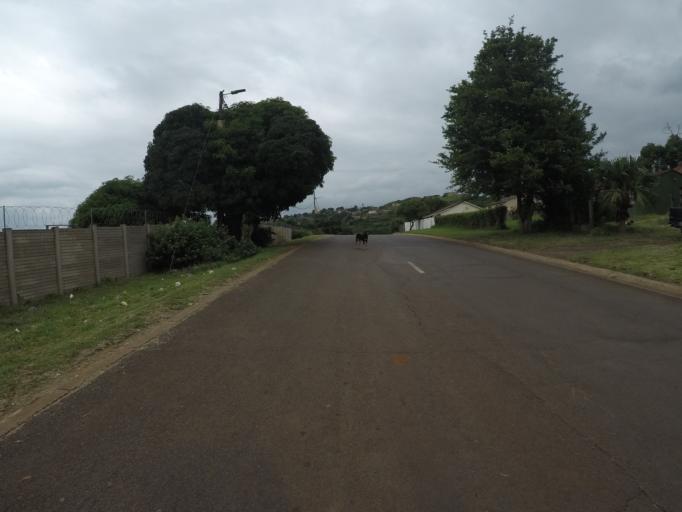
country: ZA
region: KwaZulu-Natal
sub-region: uThungulu District Municipality
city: Empangeni
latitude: -28.7722
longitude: 31.8626
